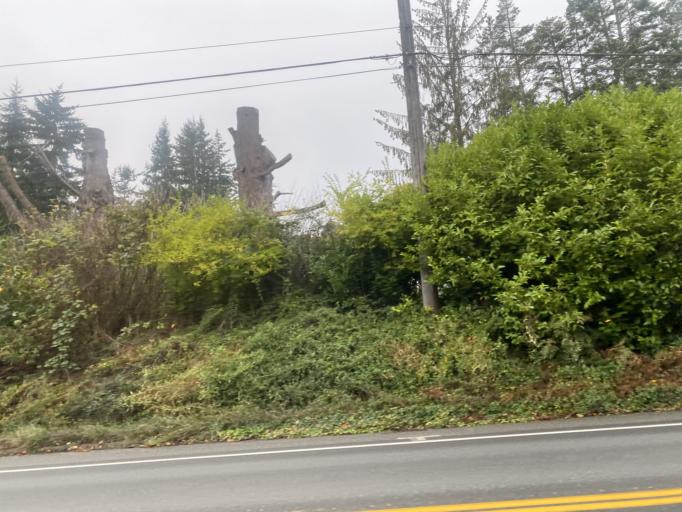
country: US
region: Washington
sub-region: Island County
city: Camano
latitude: 48.0960
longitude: -122.5719
